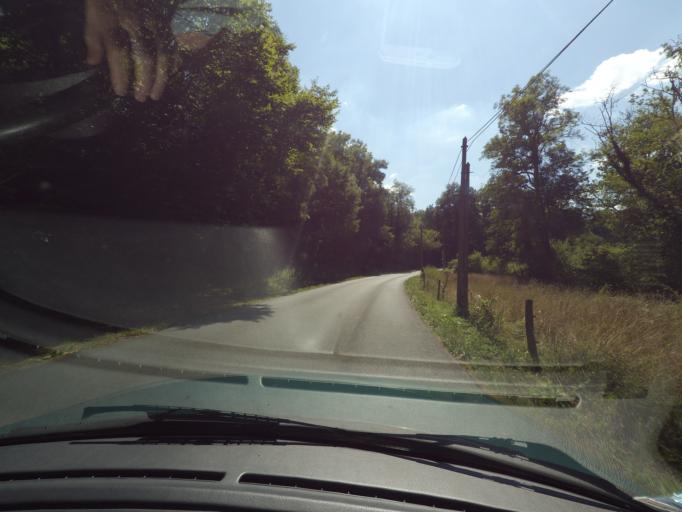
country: FR
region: Limousin
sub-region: Departement de la Haute-Vienne
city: Bosmie-l'Aiguille
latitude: 45.7744
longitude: 1.1881
